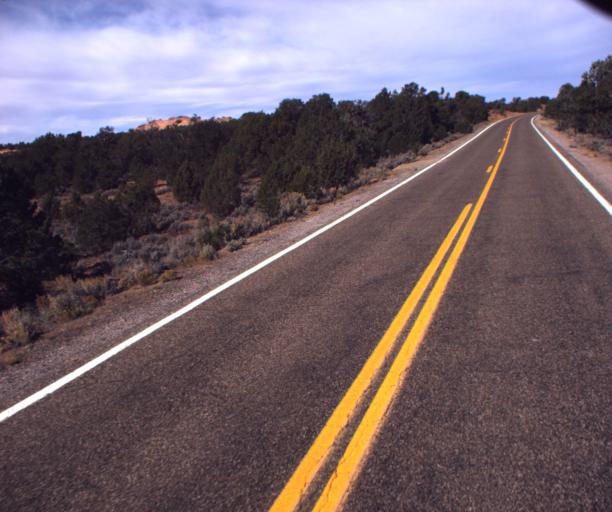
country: US
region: Arizona
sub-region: Navajo County
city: Kayenta
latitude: 36.6431
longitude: -110.5146
